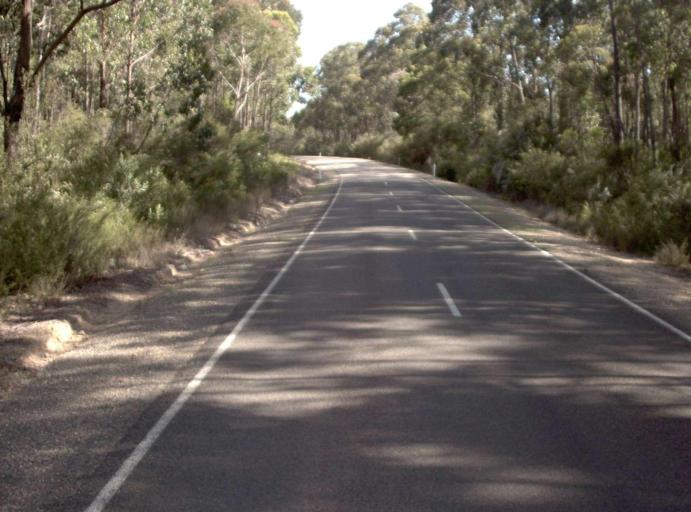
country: AU
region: Victoria
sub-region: East Gippsland
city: Lakes Entrance
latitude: -37.6384
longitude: 148.1105
